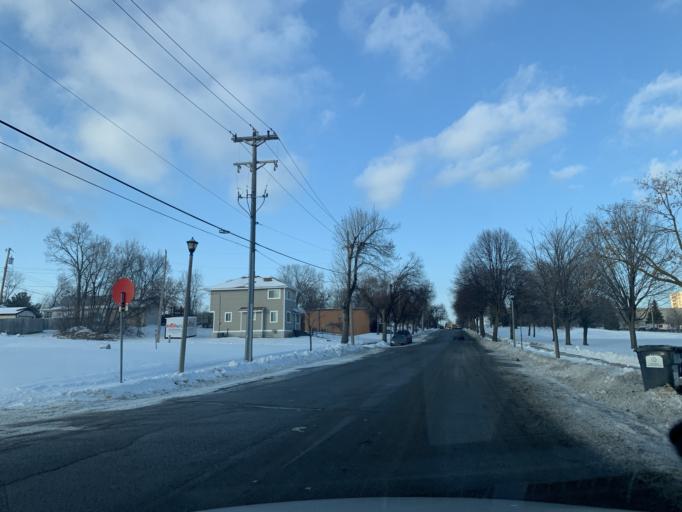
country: US
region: Minnesota
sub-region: Hennepin County
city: Minneapolis
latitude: 44.9863
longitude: -93.2982
